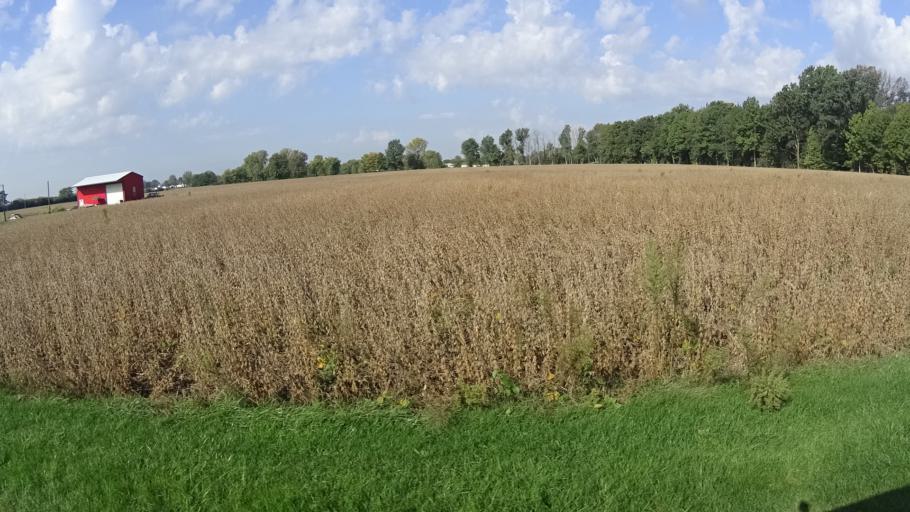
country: US
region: Indiana
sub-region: Madison County
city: Ingalls
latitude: 39.9943
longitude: -85.8243
